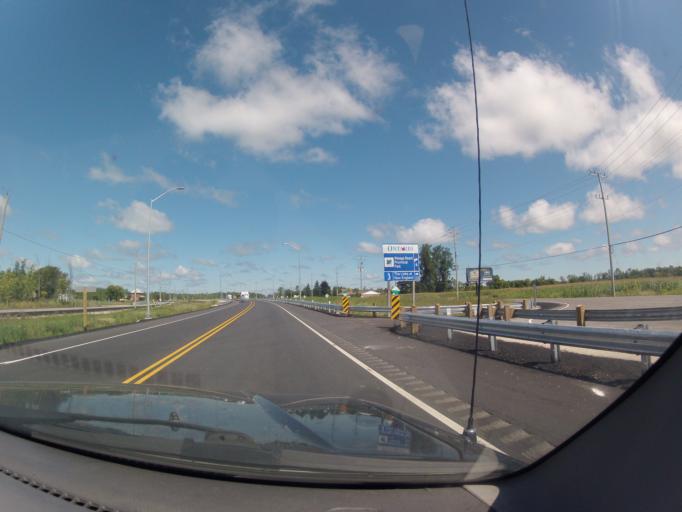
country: CA
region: Ontario
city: Wasaga Beach
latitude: 44.4548
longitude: -80.1039
